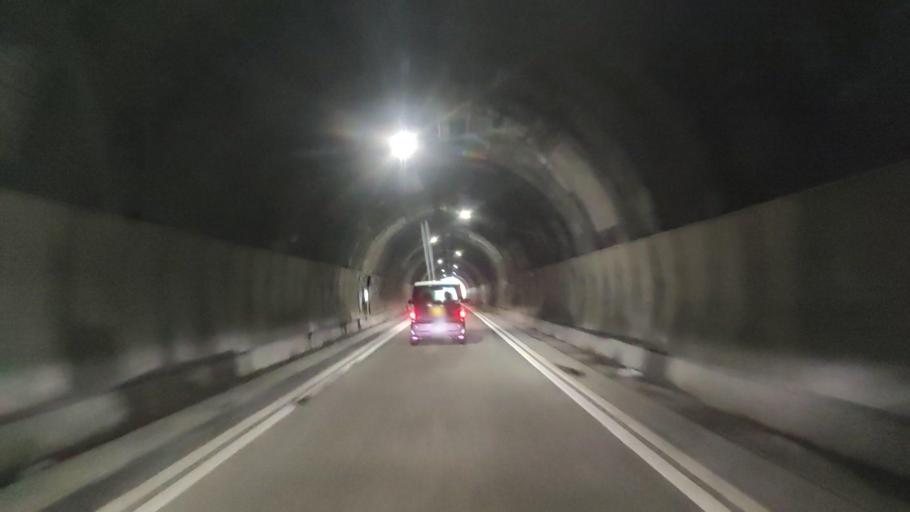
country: JP
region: Fukui
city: Takefu
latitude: 35.8462
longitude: 136.1248
